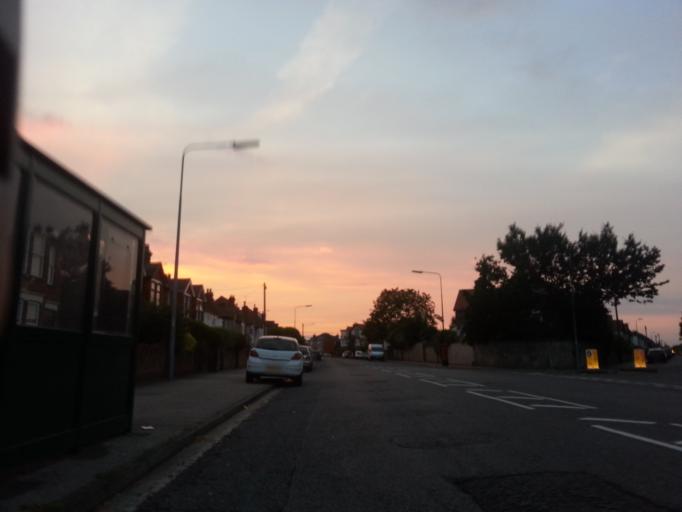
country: GB
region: England
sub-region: Suffolk
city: Ipswich
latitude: 52.0425
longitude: 1.1831
